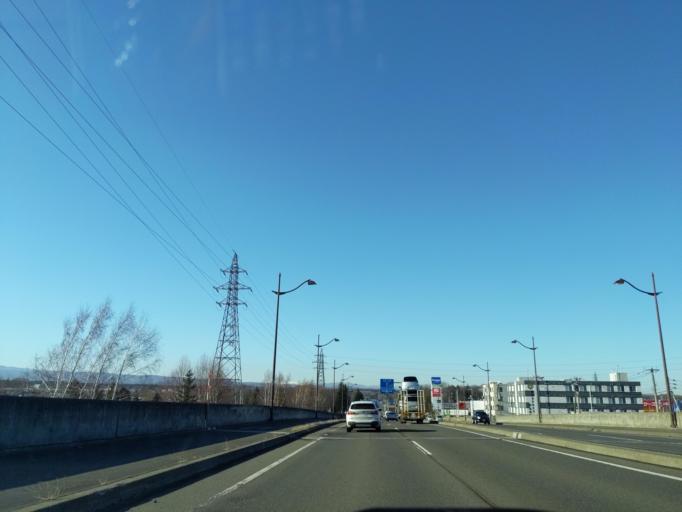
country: JP
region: Hokkaido
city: Kitahiroshima
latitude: 42.9009
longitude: 141.5736
